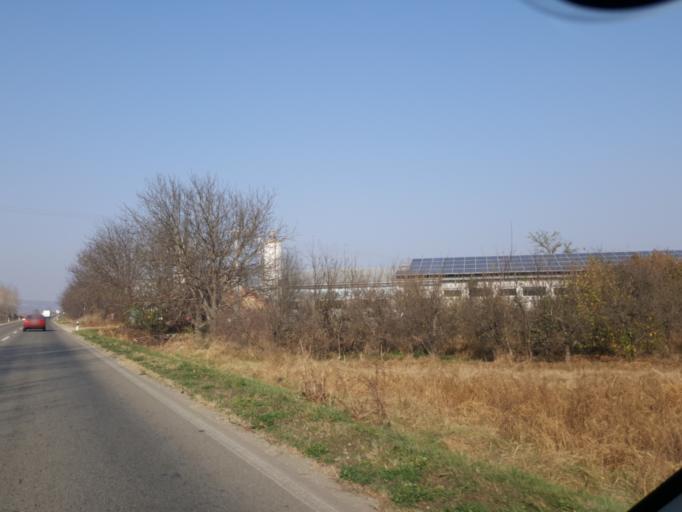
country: RS
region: Central Serbia
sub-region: Jablanicki Okrug
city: Leskovac
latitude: 43.0185
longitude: 21.9522
